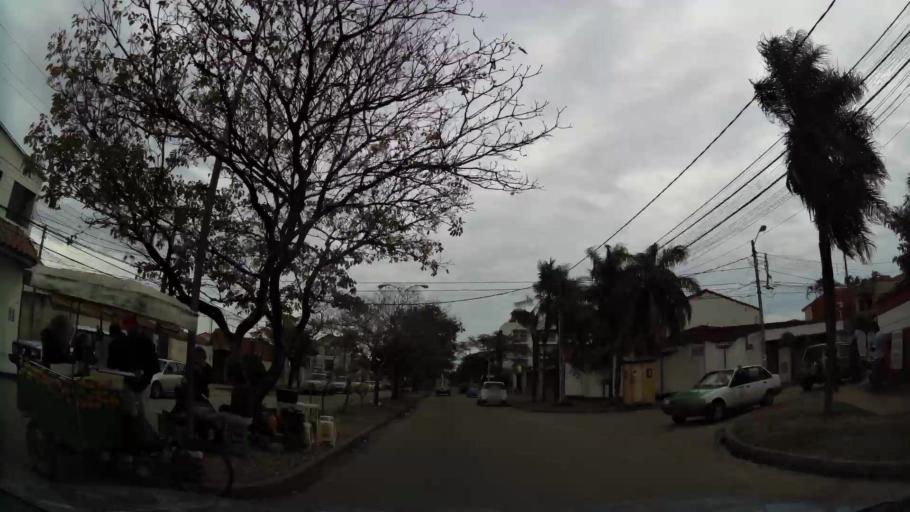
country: BO
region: Santa Cruz
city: Santa Cruz de la Sierra
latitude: -17.7786
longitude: -63.1594
